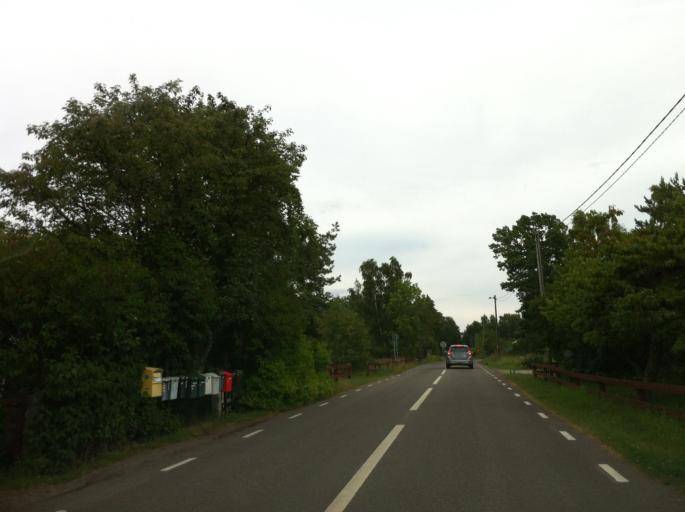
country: SE
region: Kalmar
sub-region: Vasterviks Kommun
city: Vaestervik
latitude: 57.3489
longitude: 17.0758
